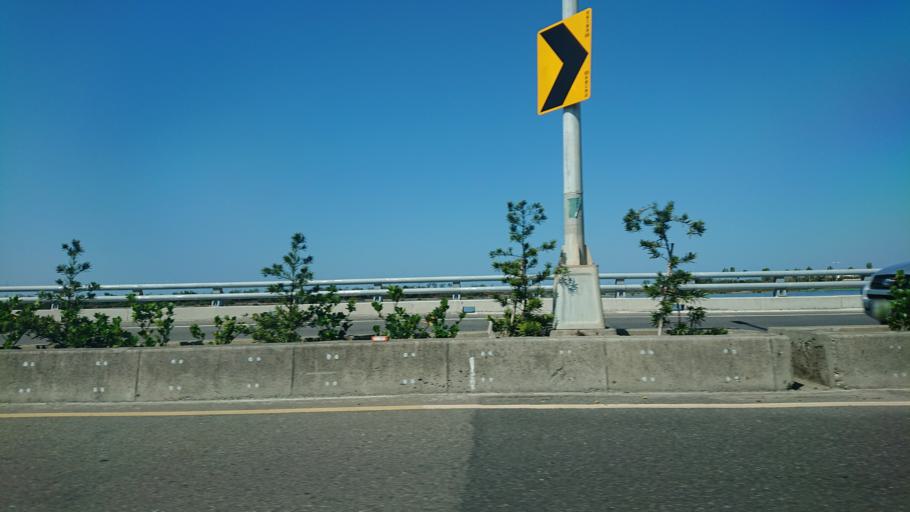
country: TW
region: Taiwan
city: Xinying
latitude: 23.2820
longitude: 120.1333
